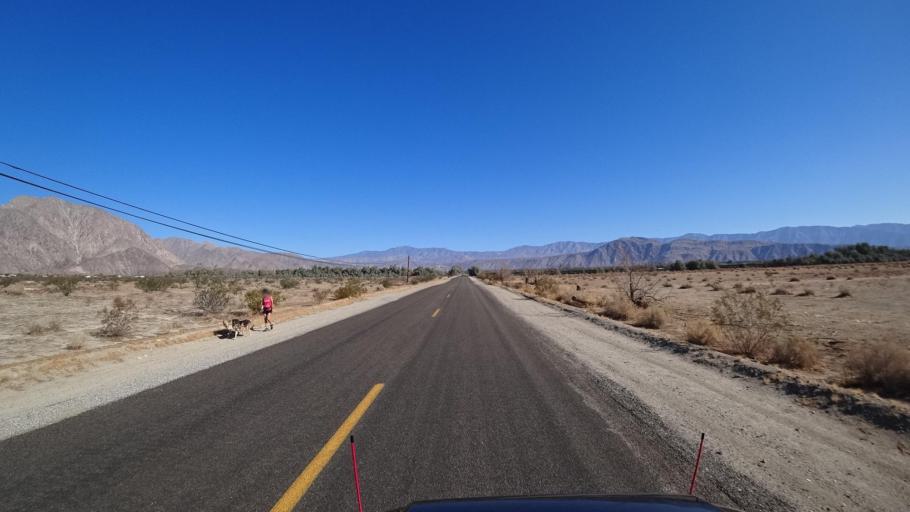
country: US
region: California
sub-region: San Diego County
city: Borrego Springs
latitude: 33.2644
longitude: -116.3750
